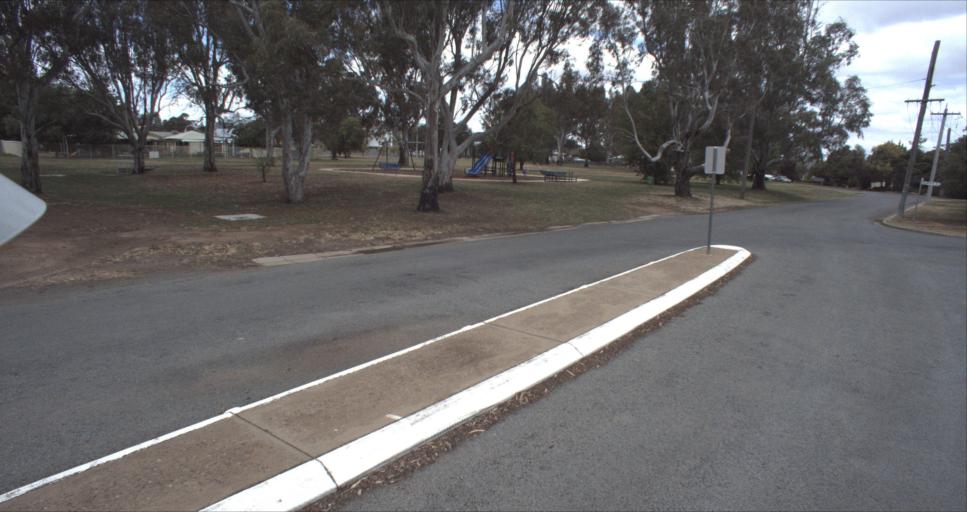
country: AU
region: New South Wales
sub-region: Leeton
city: Leeton
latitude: -34.5544
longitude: 146.3912
